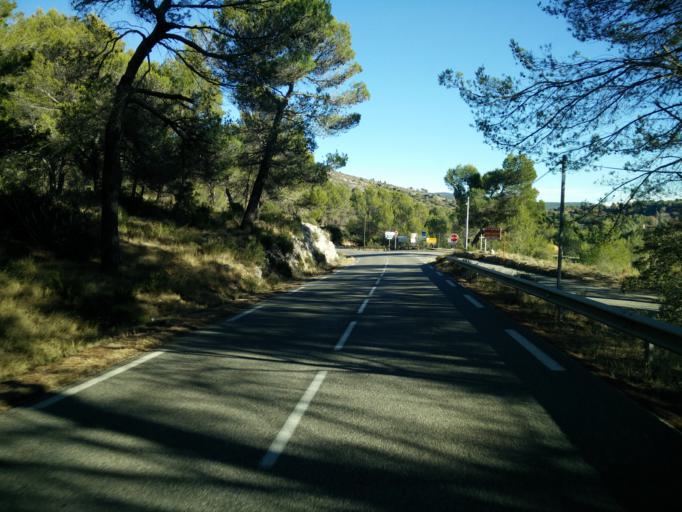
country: FR
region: Provence-Alpes-Cote d'Azur
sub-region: Departement du Var
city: Salernes
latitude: 43.5735
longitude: 6.2193
